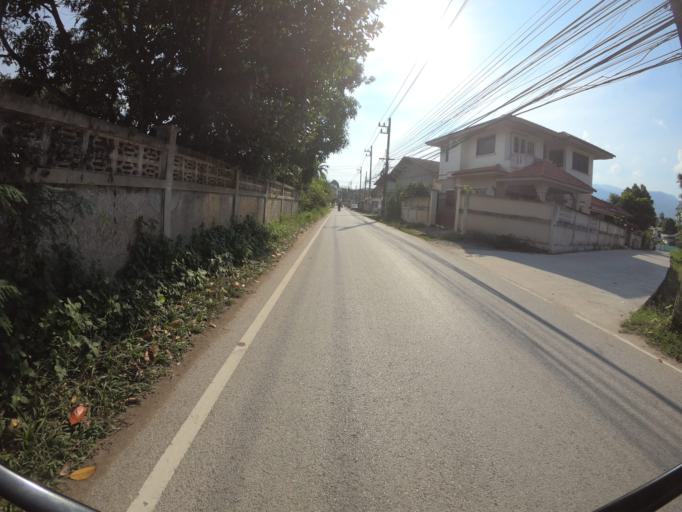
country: TH
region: Chiang Mai
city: Chiang Mai
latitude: 18.8443
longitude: 98.9766
